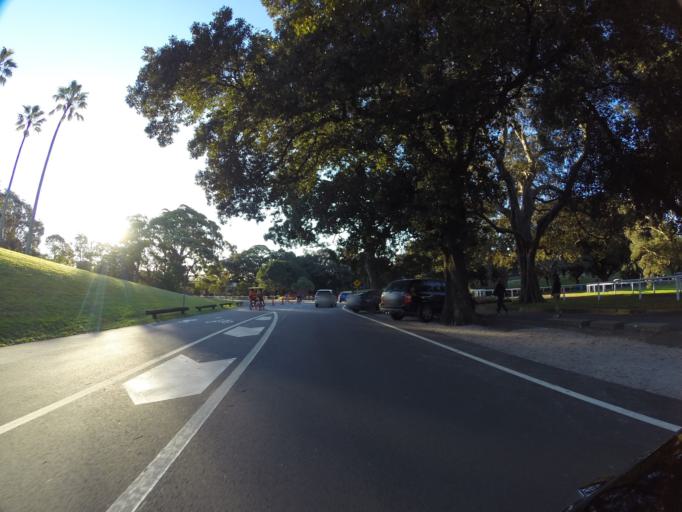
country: AU
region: New South Wales
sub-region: Woollahra
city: Woollahra
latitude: -33.8981
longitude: 151.2279
